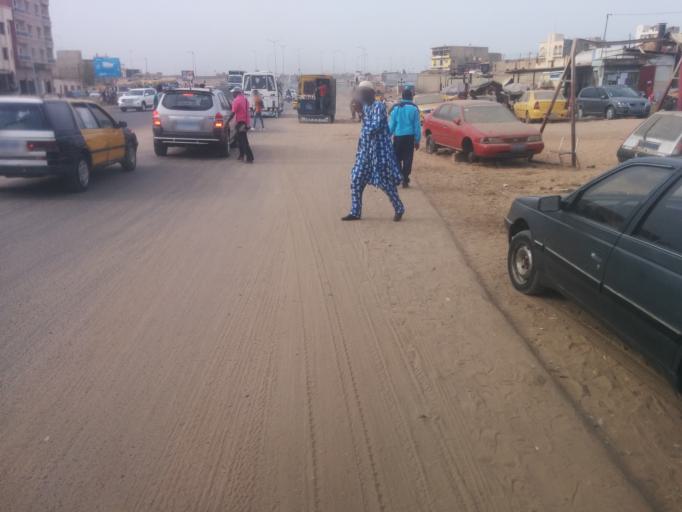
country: SN
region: Dakar
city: Grand Dakar
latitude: 14.7465
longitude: -17.4455
